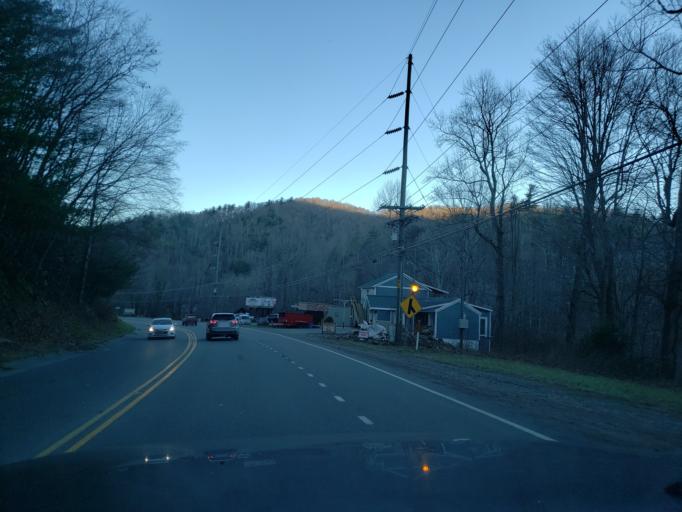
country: US
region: North Carolina
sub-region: Watauga County
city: Foscoe
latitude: 36.2045
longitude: -81.7337
